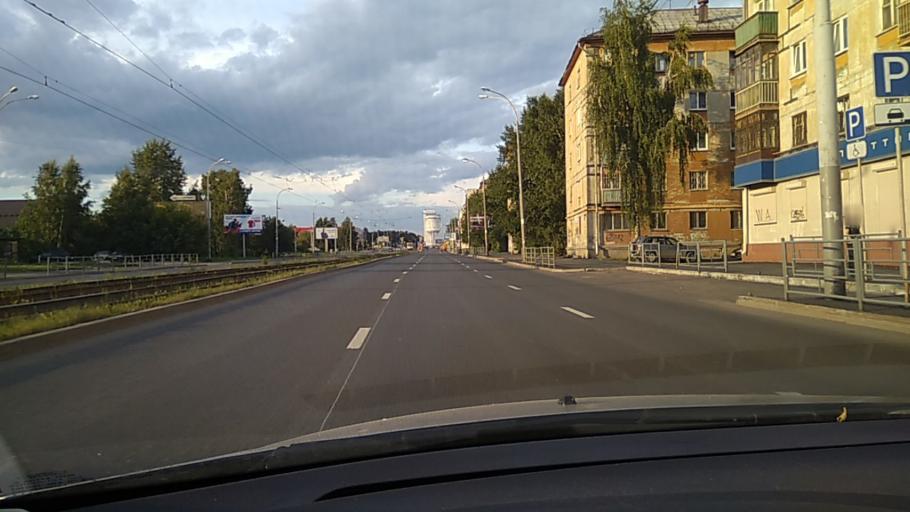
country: RU
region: Sverdlovsk
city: Yekaterinburg
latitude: 56.8883
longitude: 60.5671
